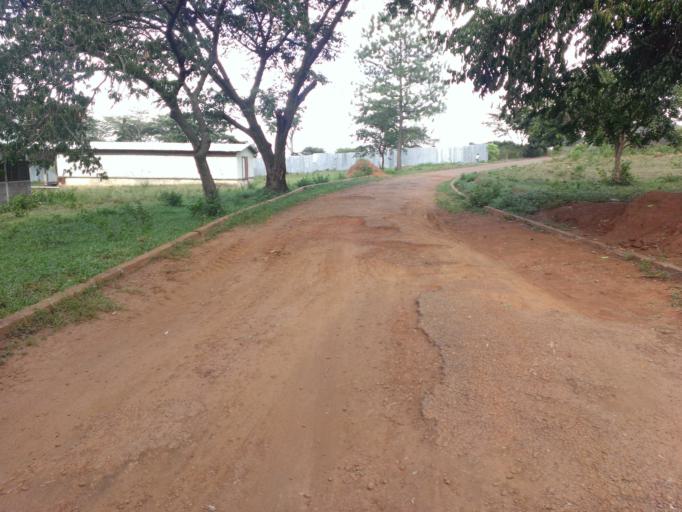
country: UG
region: Eastern Region
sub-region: Busia District
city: Busia
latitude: 0.5443
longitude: 34.0211
